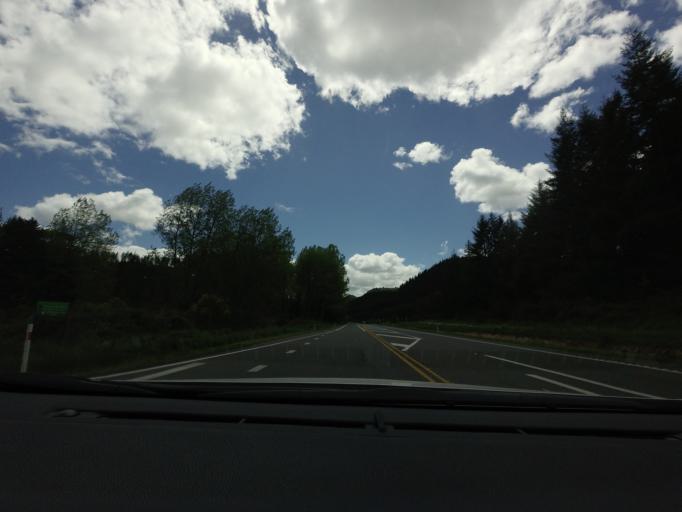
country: NZ
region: Bay of Plenty
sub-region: Rotorua District
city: Rotorua
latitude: -38.2261
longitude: 176.2912
